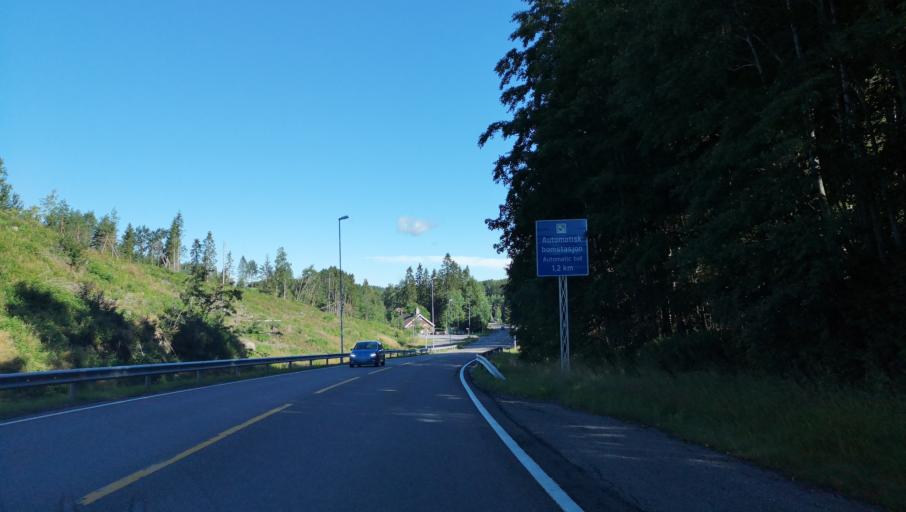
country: NO
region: Ostfold
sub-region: Spydeberg
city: Spydeberg
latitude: 59.5986
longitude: 11.1034
